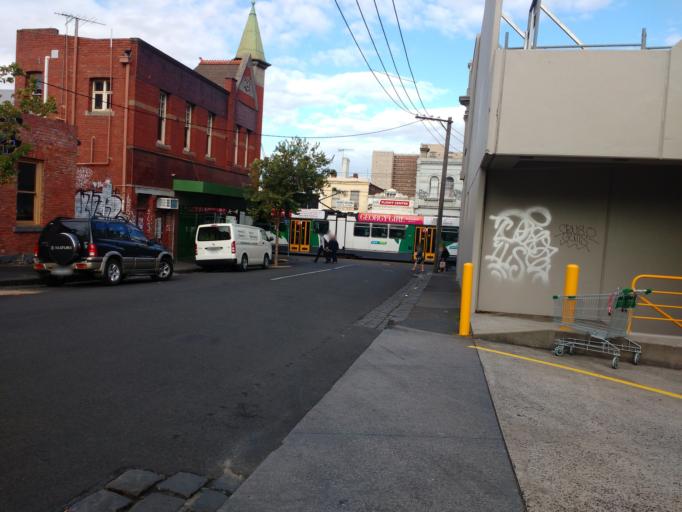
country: AU
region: Victoria
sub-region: Yarra
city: Collingwood
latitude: -37.8012
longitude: 144.9834
